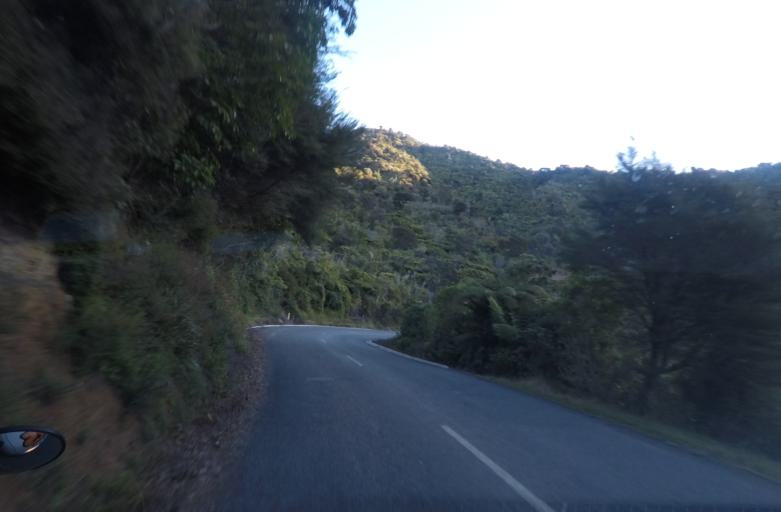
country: NZ
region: Marlborough
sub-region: Marlborough District
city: Picton
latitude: -41.2733
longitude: 173.9595
